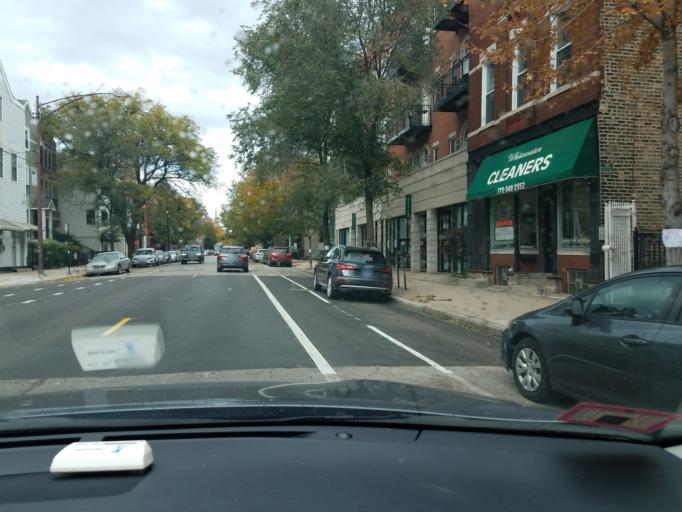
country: US
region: Illinois
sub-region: Cook County
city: Chicago
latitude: 41.9278
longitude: -87.6634
